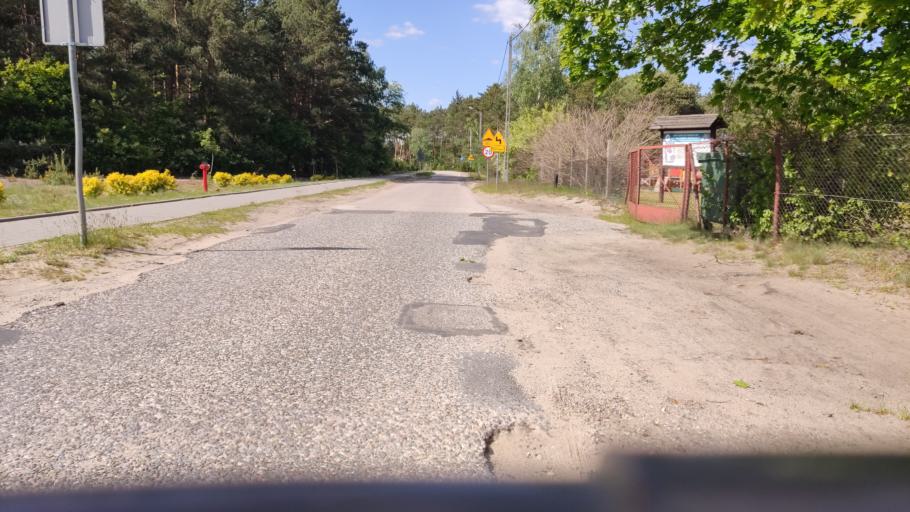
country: PL
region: Kujawsko-Pomorskie
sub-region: Wloclawek
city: Wloclawek
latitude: 52.5943
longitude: 19.0871
